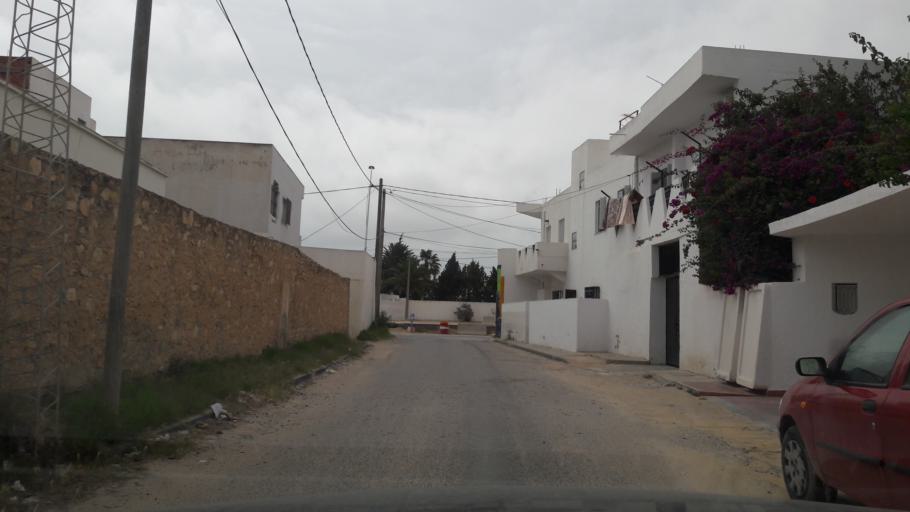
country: TN
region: Safaqis
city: Sfax
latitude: 34.7715
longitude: 10.7565
